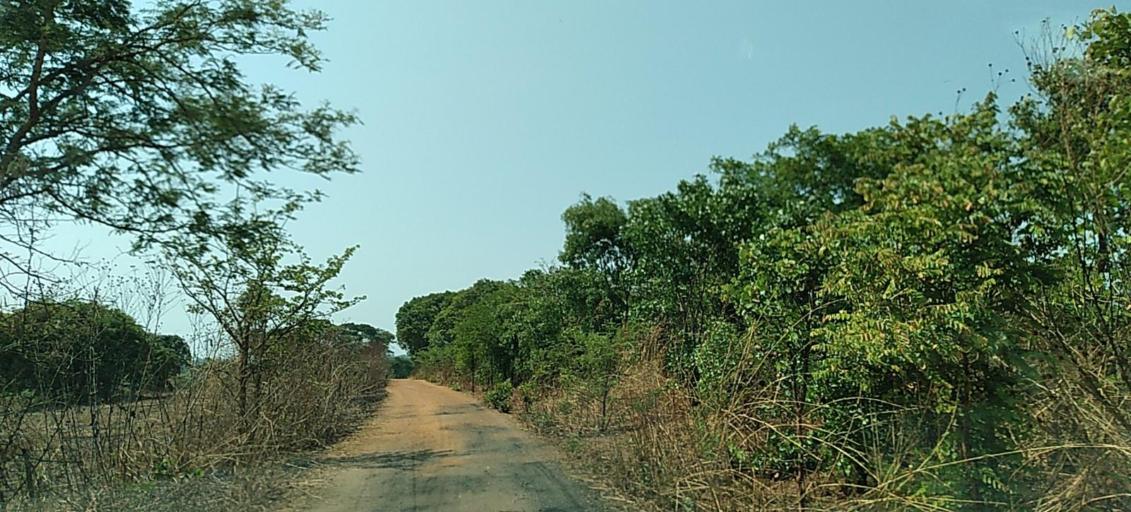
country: ZM
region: Copperbelt
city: Luanshya
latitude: -13.3443
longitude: 28.3925
